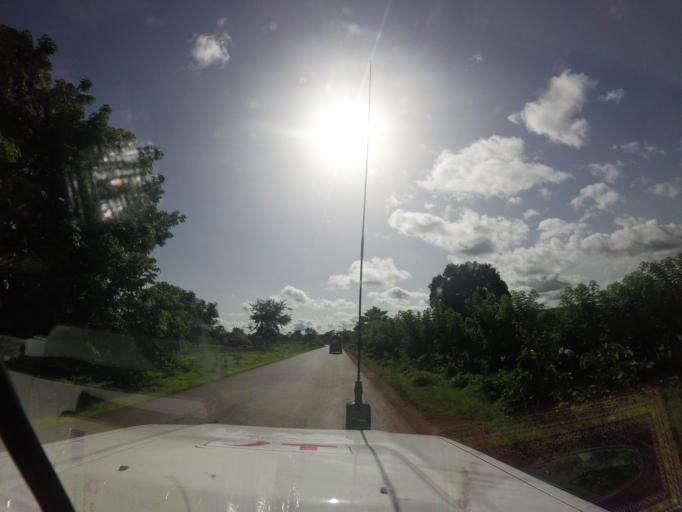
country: GN
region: Mamou
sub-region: Mamou Prefecture
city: Mamou
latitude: 10.2970
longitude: -12.3673
